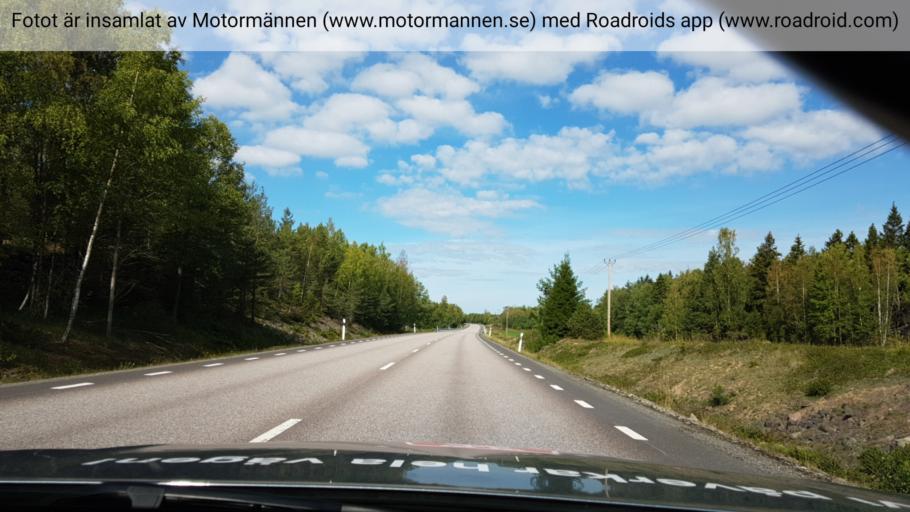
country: SE
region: Uppsala
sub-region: Osthammars Kommun
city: Bjorklinge
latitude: 59.9717
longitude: 17.3655
